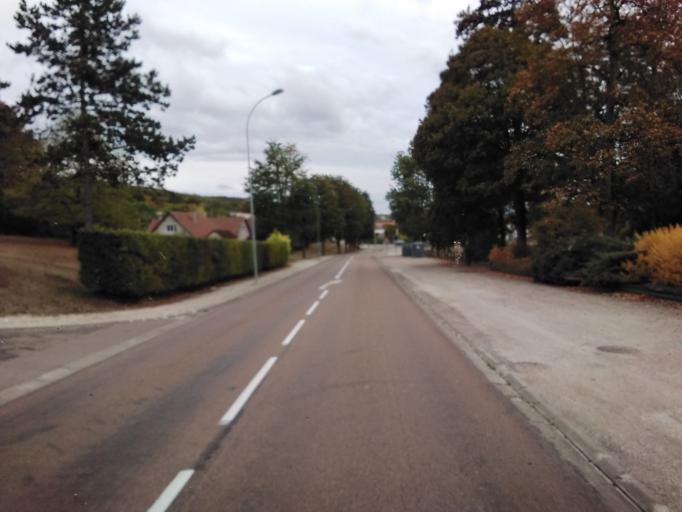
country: FR
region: Champagne-Ardenne
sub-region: Departement de l'Aube
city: Bar-sur-Seine
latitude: 48.1181
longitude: 4.3855
